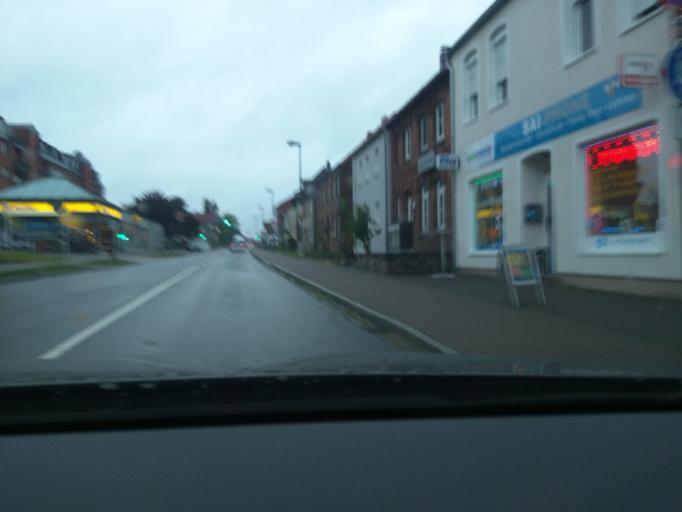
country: DE
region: Schleswig-Holstein
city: Lauenburg
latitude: 53.3746
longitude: 10.5575
